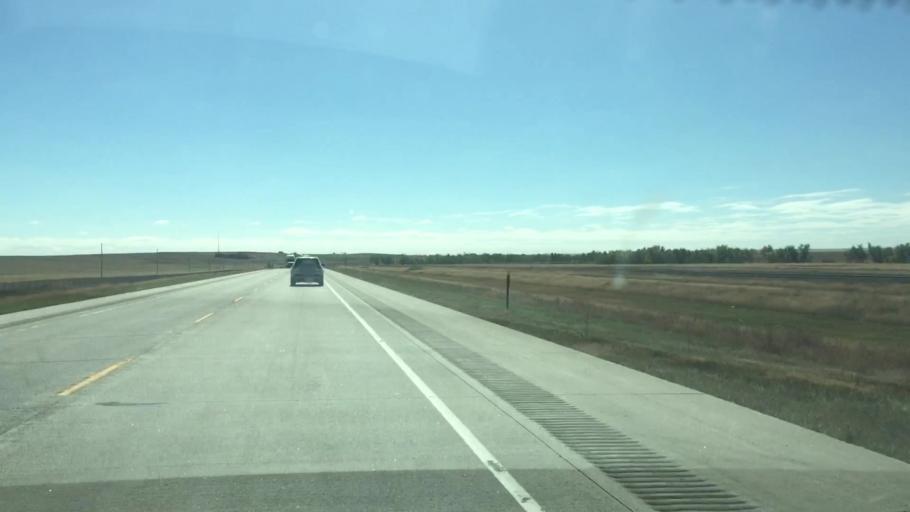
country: US
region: Colorado
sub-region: Lincoln County
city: Limon
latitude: 39.2291
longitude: -103.6148
